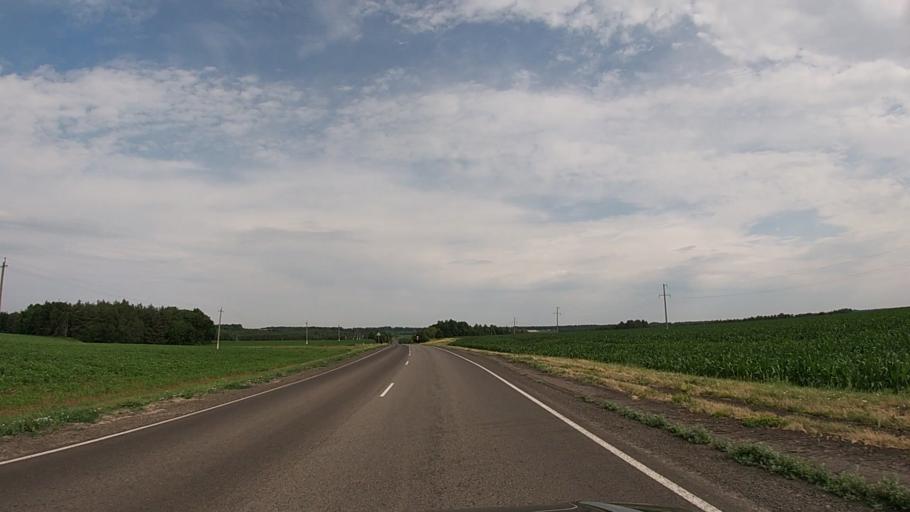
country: RU
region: Belgorod
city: Krasnaya Yaruga
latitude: 50.8209
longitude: 35.5015
